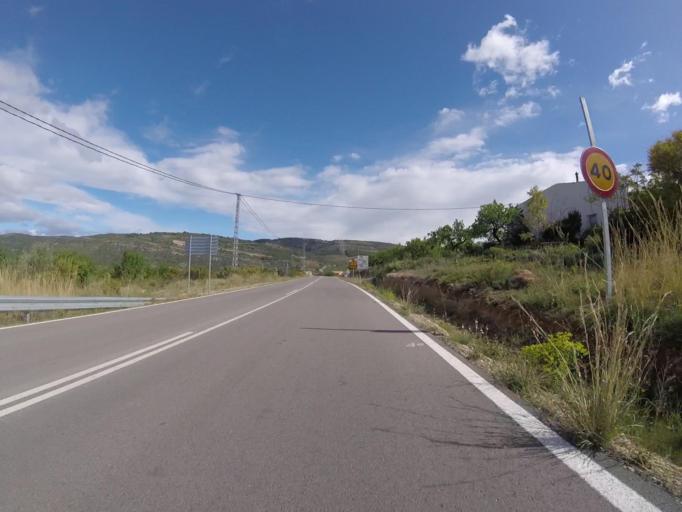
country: ES
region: Valencia
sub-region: Provincia de Castello
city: Culla
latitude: 40.2807
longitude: -0.1120
